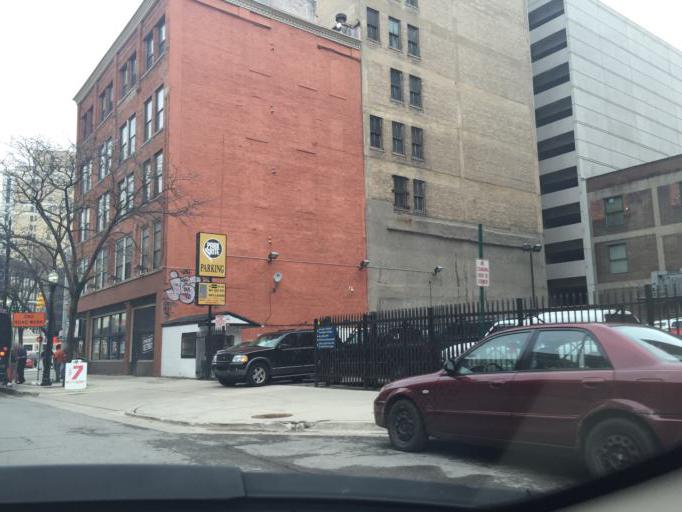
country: US
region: Michigan
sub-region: Wayne County
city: Detroit
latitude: 42.3332
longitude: -83.0494
